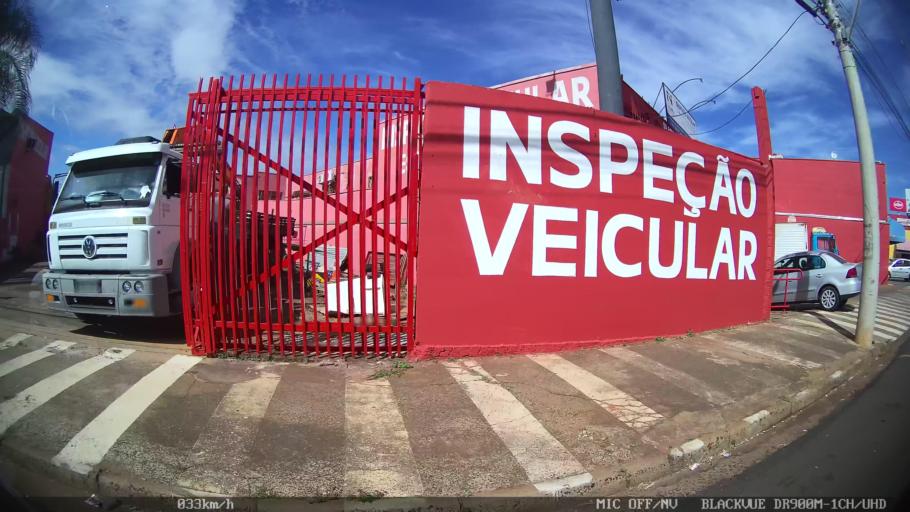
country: BR
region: Sao Paulo
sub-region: Sao Jose Do Rio Preto
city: Sao Jose do Rio Preto
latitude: -20.8288
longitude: -49.3592
